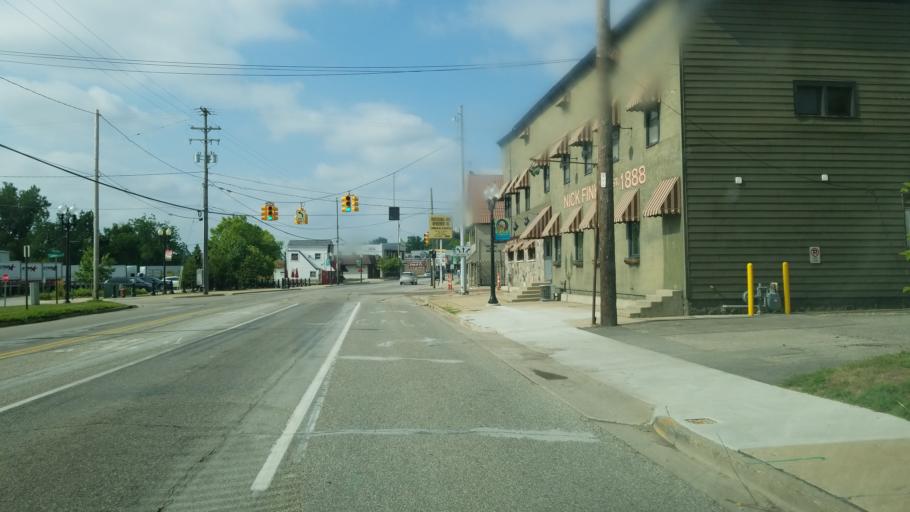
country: US
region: Michigan
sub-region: Kent County
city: Comstock Park
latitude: 43.0347
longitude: -85.6654
